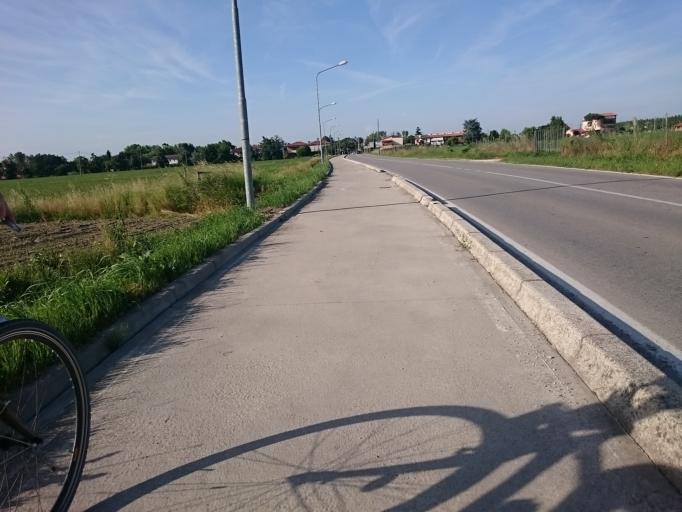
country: IT
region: Veneto
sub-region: Provincia di Padova
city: Terradura
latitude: 45.3541
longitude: 11.8212
